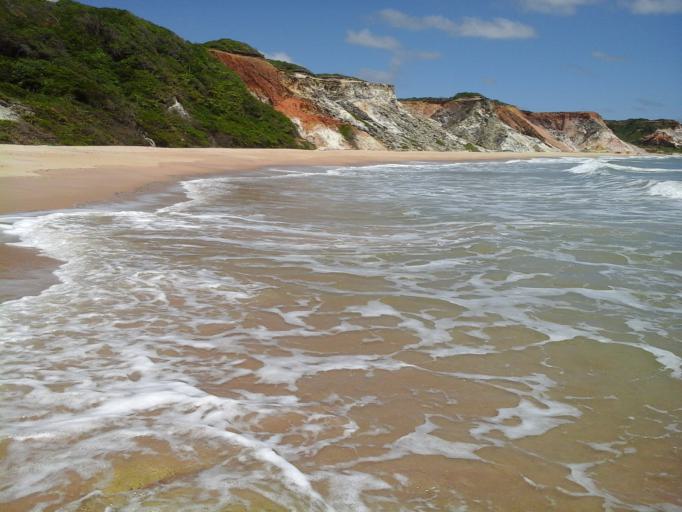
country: BR
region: Paraiba
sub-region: Pitimbu
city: Pitimbu
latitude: -7.3627
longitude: -34.7992
